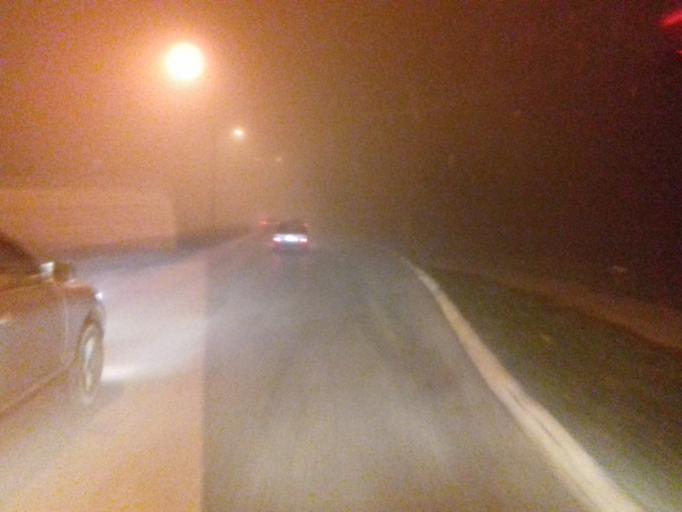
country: BA
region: Federation of Bosnia and Herzegovina
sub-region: Kanton Sarajevo
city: Sarajevo
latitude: 43.8317
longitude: 18.3516
